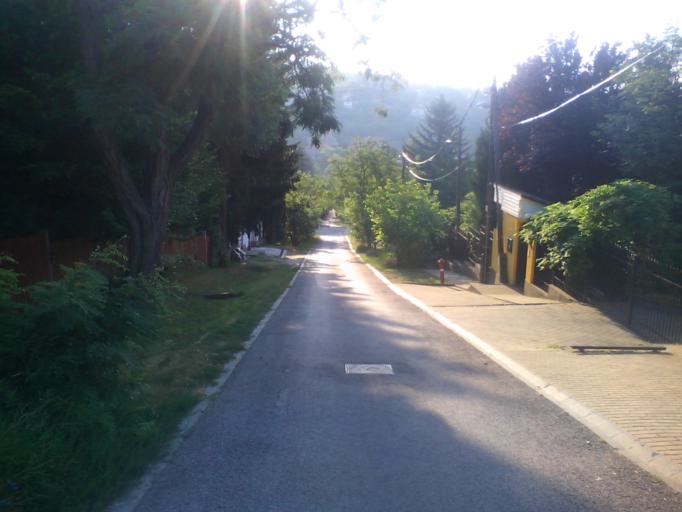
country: HU
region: Pest
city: Solymar
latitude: 47.5513
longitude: 18.9458
